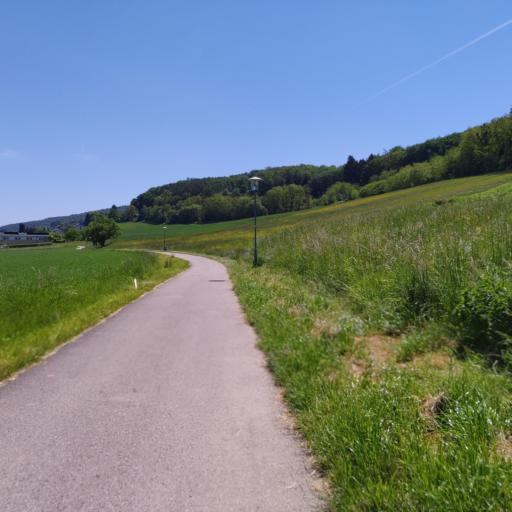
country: AT
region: Lower Austria
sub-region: Politischer Bezirk Sankt Polten
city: Maria-Anzbach
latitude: 48.1885
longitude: 15.9369
